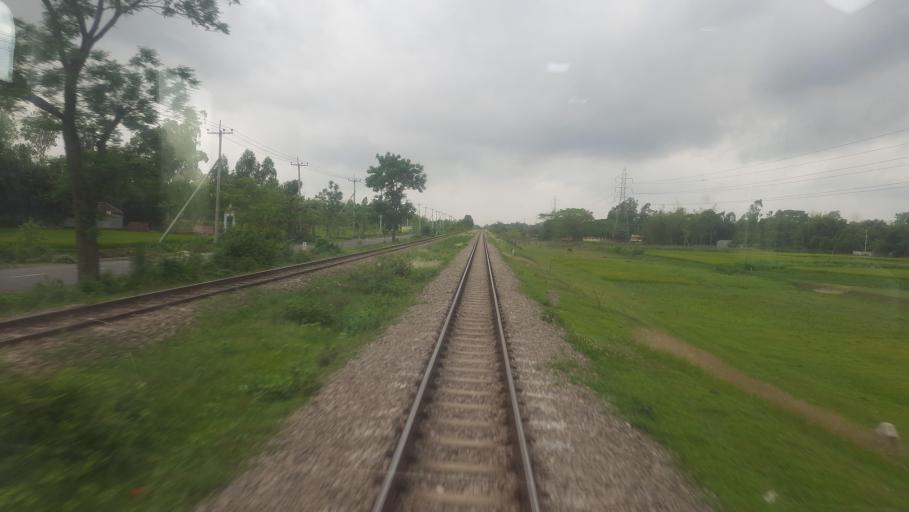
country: BD
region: Dhaka
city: Narsingdi
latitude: 23.9837
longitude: 90.8487
